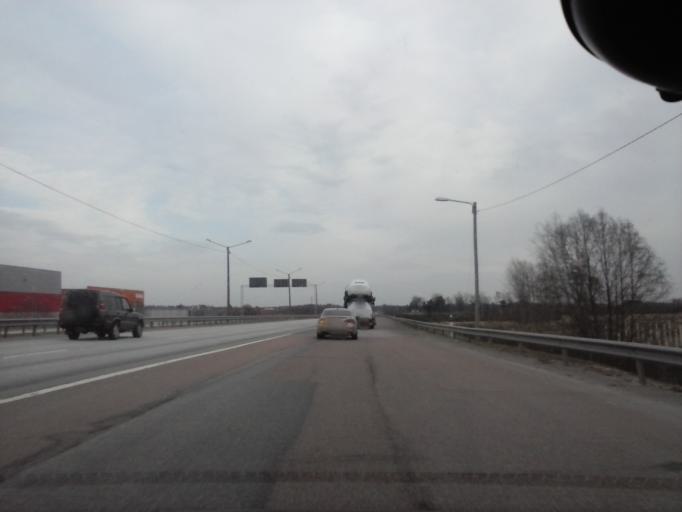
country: EE
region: Harju
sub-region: Rae vald
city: Jueri
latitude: 59.3499
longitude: 24.8872
